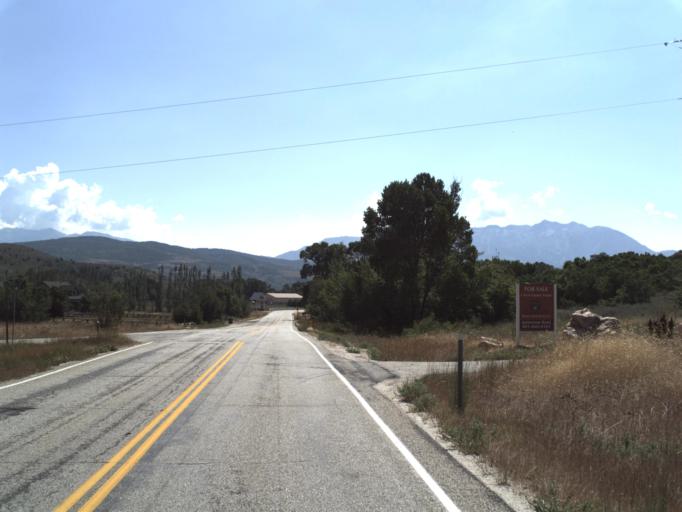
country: US
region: Utah
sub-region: Weber County
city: Wolf Creek
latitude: 41.2642
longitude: -111.6947
